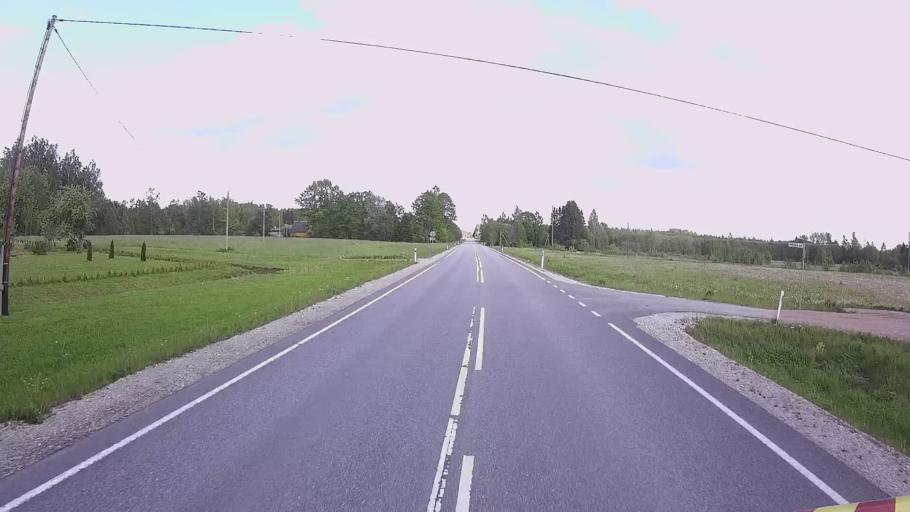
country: EE
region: Jogevamaa
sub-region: Mustvee linn
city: Mustvee
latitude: 58.8697
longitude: 26.8279
